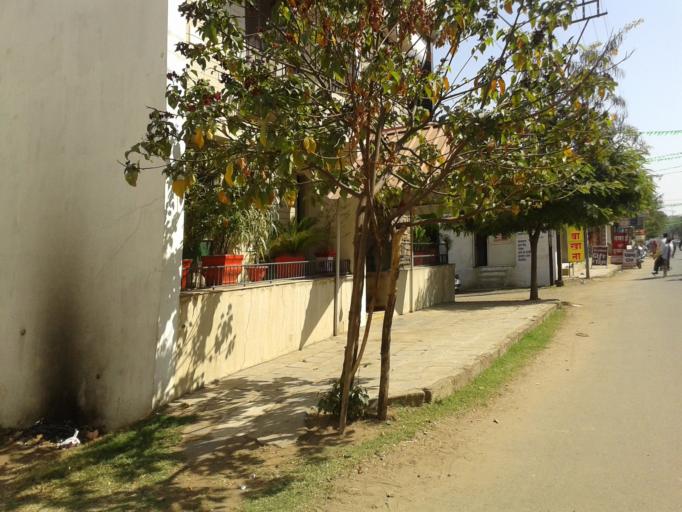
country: IN
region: Maharashtra
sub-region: Gondiya
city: Gondia
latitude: 21.4640
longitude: 80.1916
